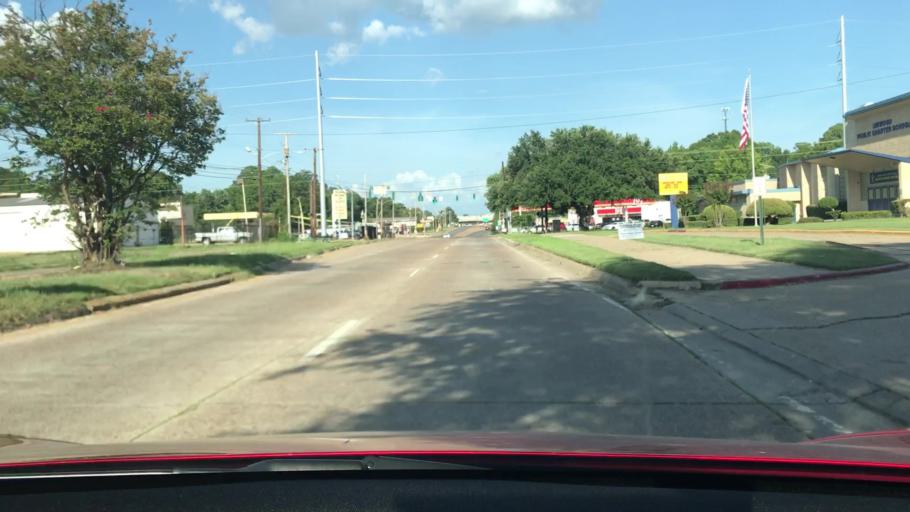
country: US
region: Louisiana
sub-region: Bossier Parish
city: Bossier City
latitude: 32.4420
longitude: -93.7645
